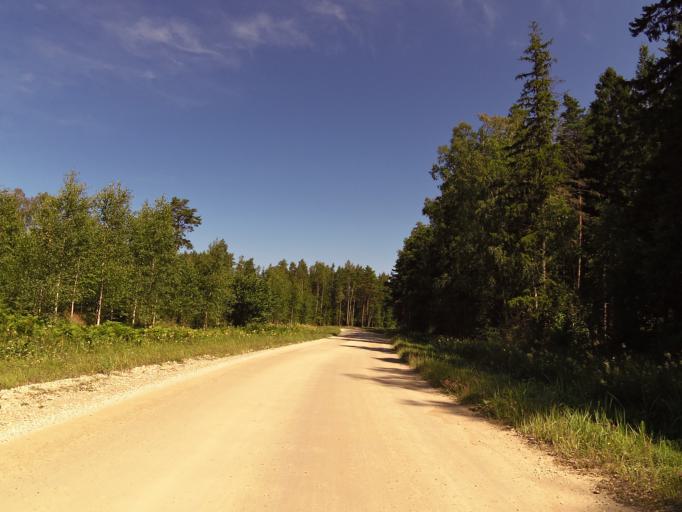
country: EE
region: Hiiumaa
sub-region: Kaerdla linn
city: Kardla
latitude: 58.9288
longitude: 22.3720
